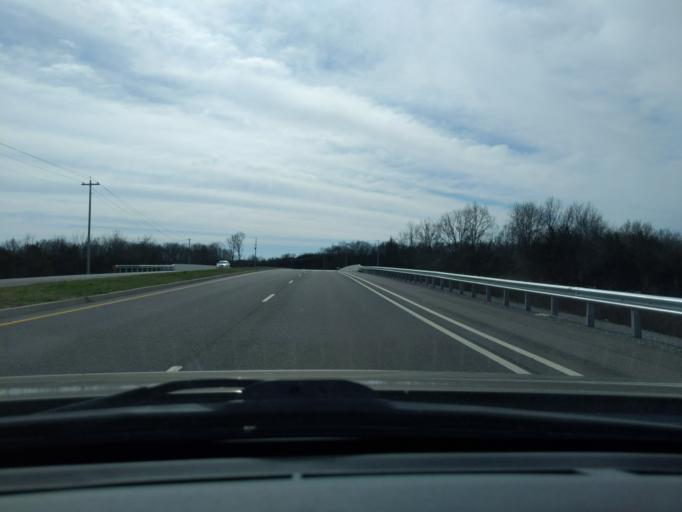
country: US
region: Tennessee
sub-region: Wilson County
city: Mount Juliet
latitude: 36.1955
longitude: -86.4796
